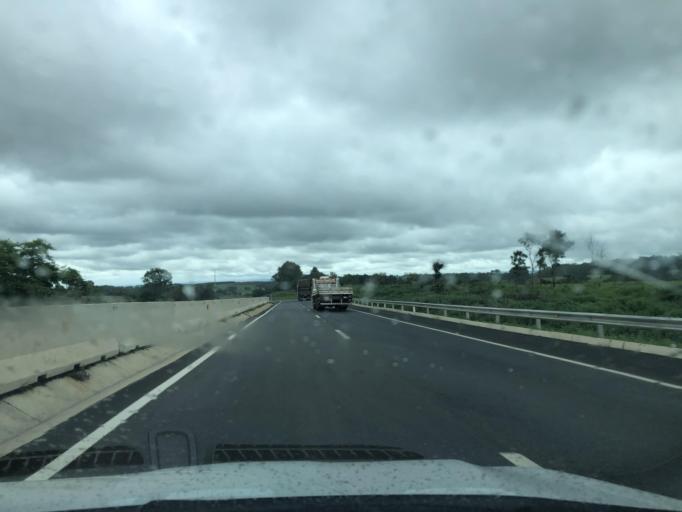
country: BR
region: Goias
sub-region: Catalao
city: Catalao
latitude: -18.2648
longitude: -47.9998
